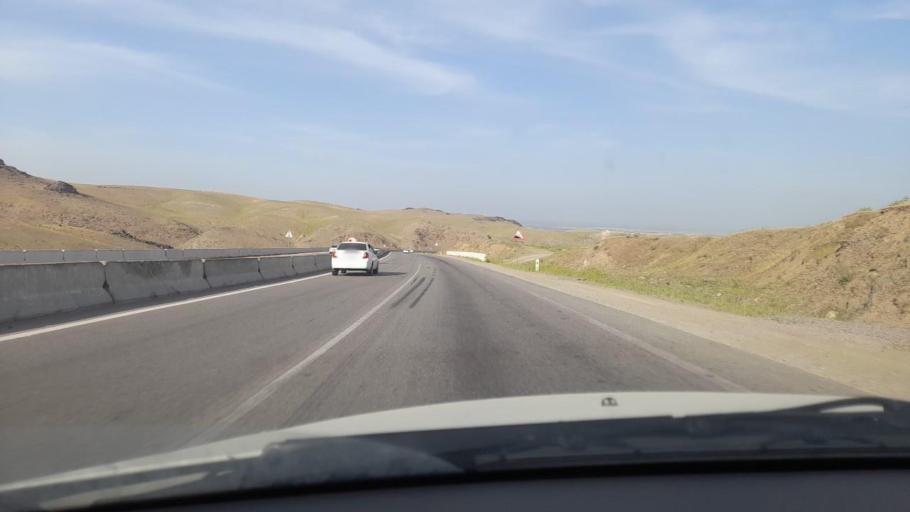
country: UZ
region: Jizzax
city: Jizzax
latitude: 40.0514
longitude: 67.7775
